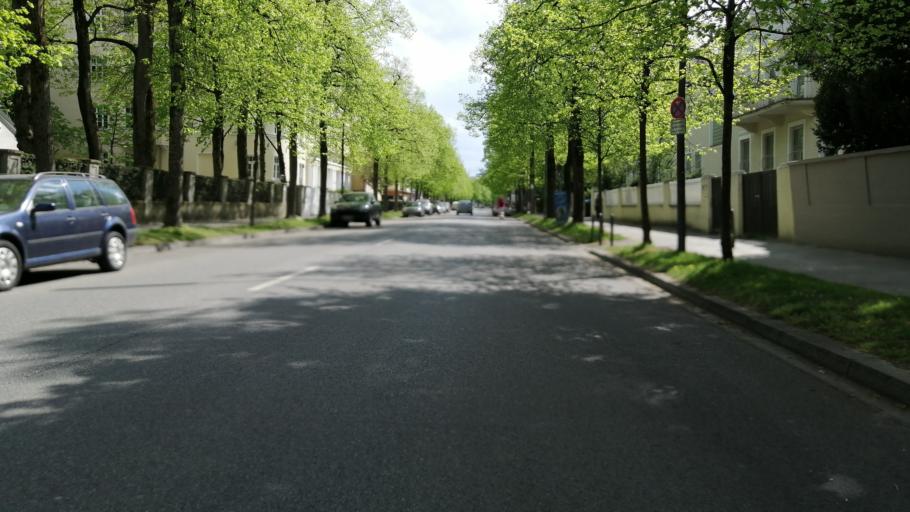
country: DE
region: Bavaria
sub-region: Upper Bavaria
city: Bogenhausen
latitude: 48.1425
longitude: 11.6067
